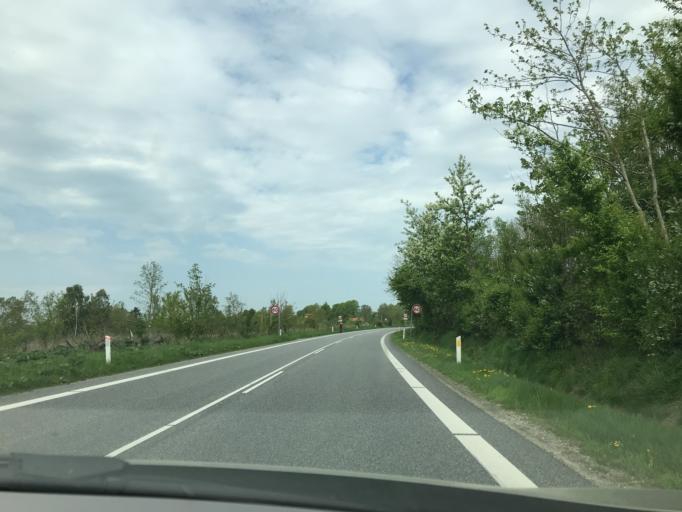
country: DK
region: South Denmark
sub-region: Assens Kommune
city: Assens
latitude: 55.3225
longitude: 9.9369
